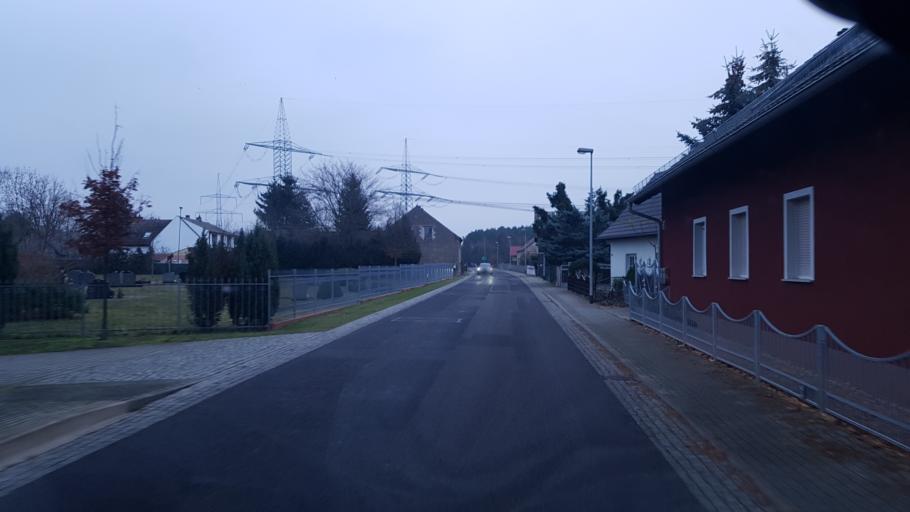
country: DE
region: Brandenburg
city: Guhrow
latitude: 51.8520
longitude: 14.2221
